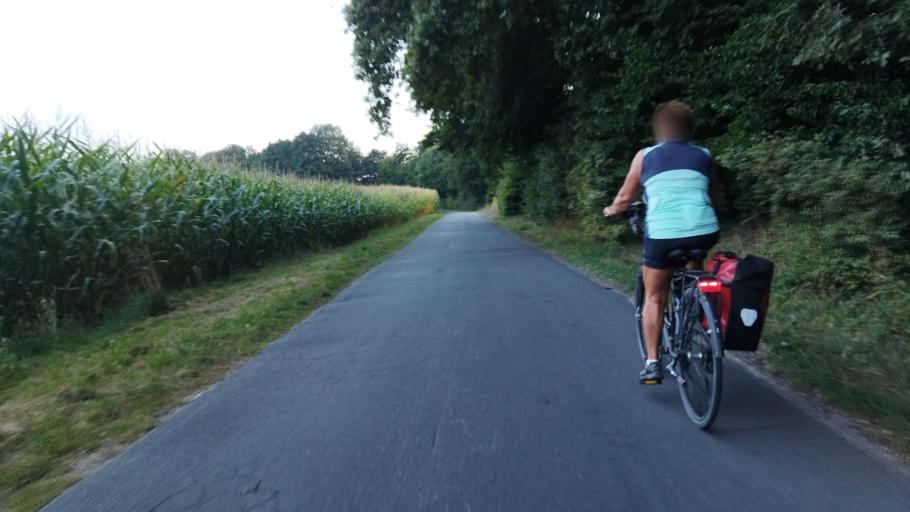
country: DE
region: Lower Saxony
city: Bad Laer
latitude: 52.1171
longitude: 8.0554
